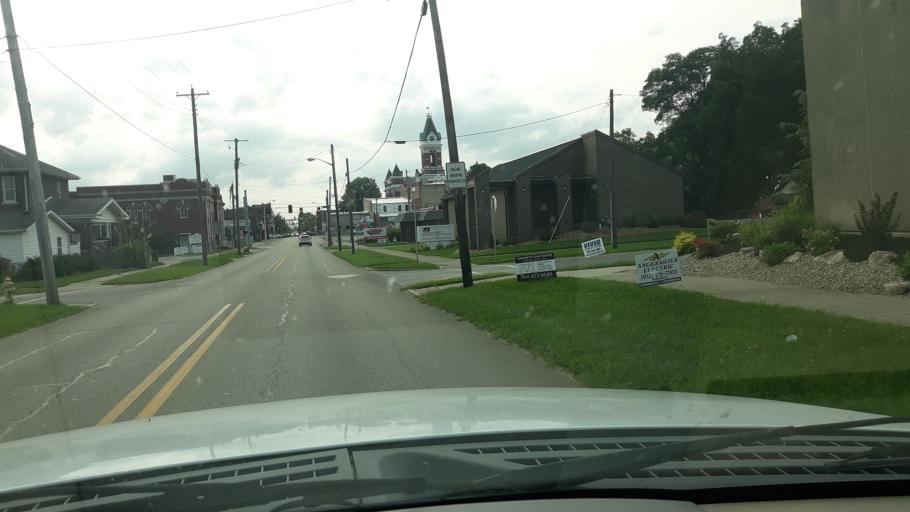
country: US
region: Indiana
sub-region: Gibson County
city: Princeton
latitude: 38.3552
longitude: -87.5647
